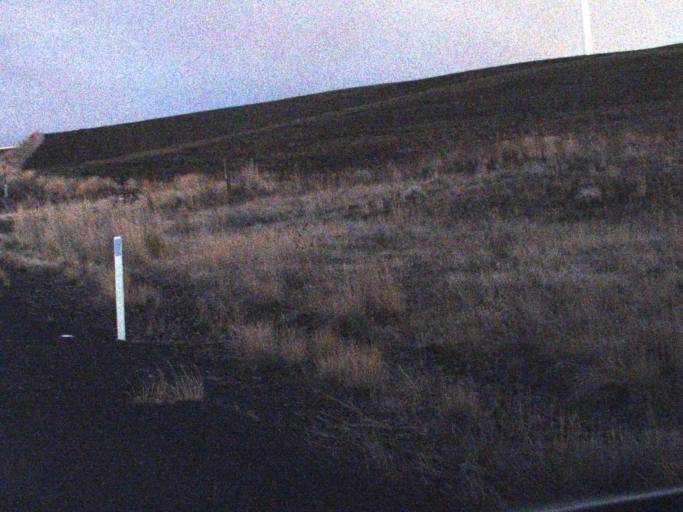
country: US
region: Washington
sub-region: Garfield County
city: Pomeroy
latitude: 46.5862
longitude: -117.7794
